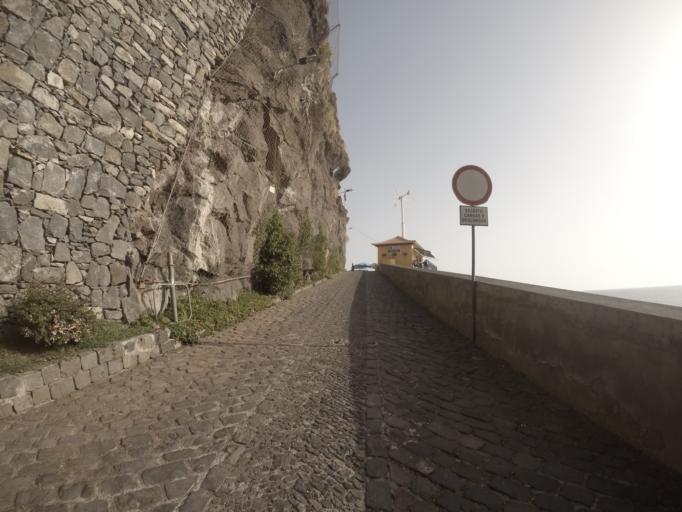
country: PT
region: Madeira
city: Ponta do Sol
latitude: 32.6789
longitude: -17.1040
